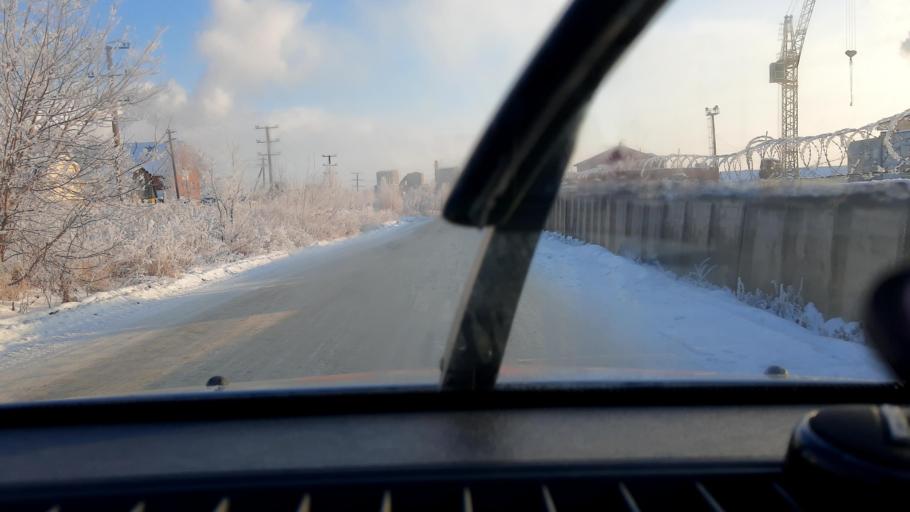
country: RU
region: Bashkortostan
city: Iglino
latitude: 54.7705
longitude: 56.2439
